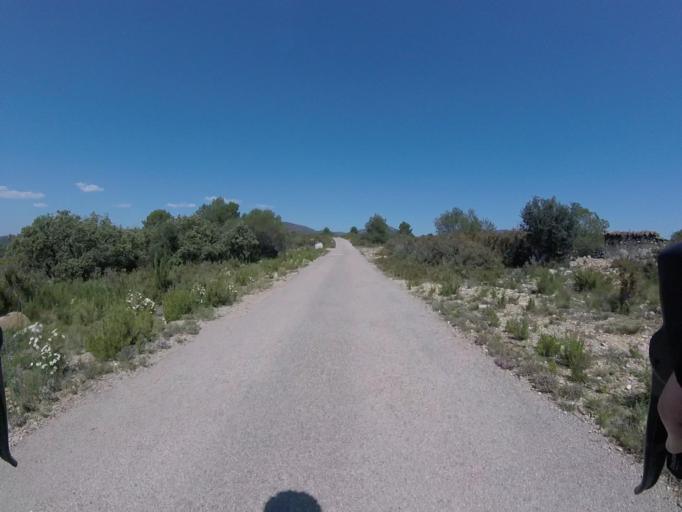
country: ES
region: Valencia
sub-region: Provincia de Castello
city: Sierra-Engarceran
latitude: 40.2263
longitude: -0.0225
